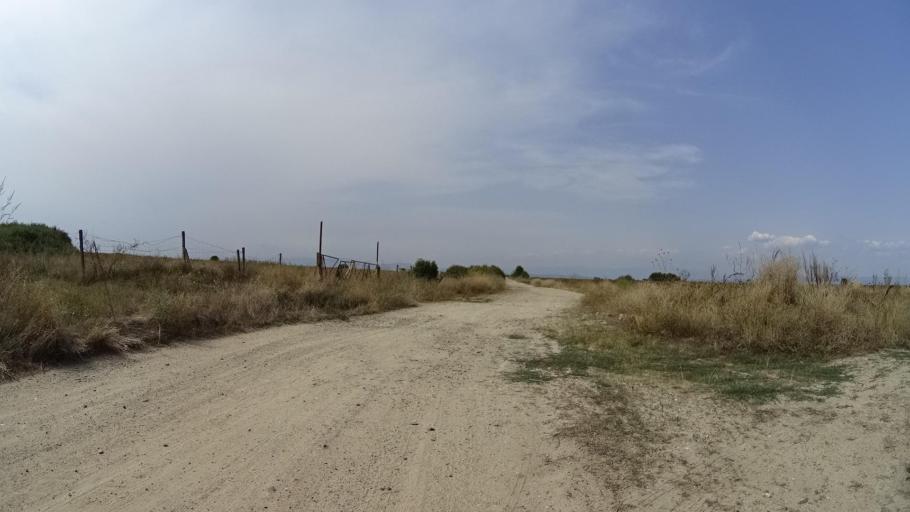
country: BG
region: Plovdiv
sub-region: Obshtina Kaloyanovo
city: Kaloyanovo
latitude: 42.2820
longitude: 24.7986
